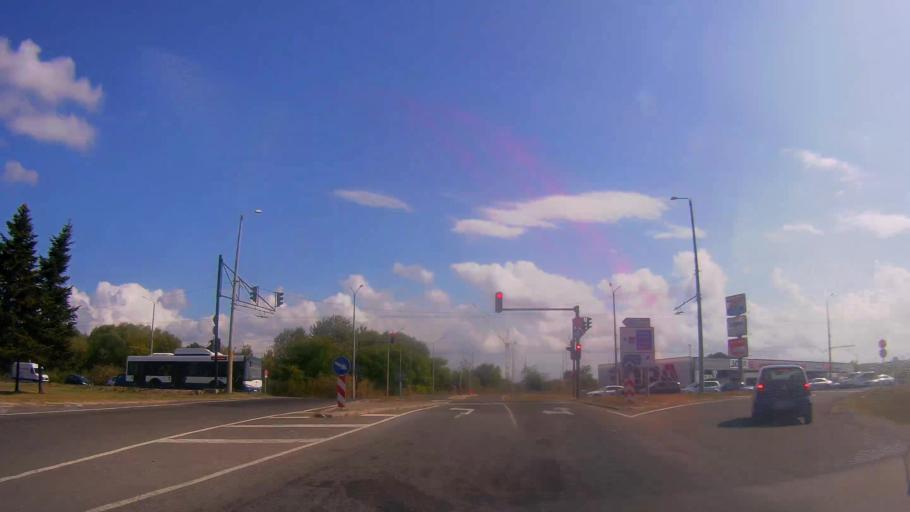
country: BG
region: Burgas
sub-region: Obshtina Burgas
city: Burgas
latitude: 42.4726
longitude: 27.4264
